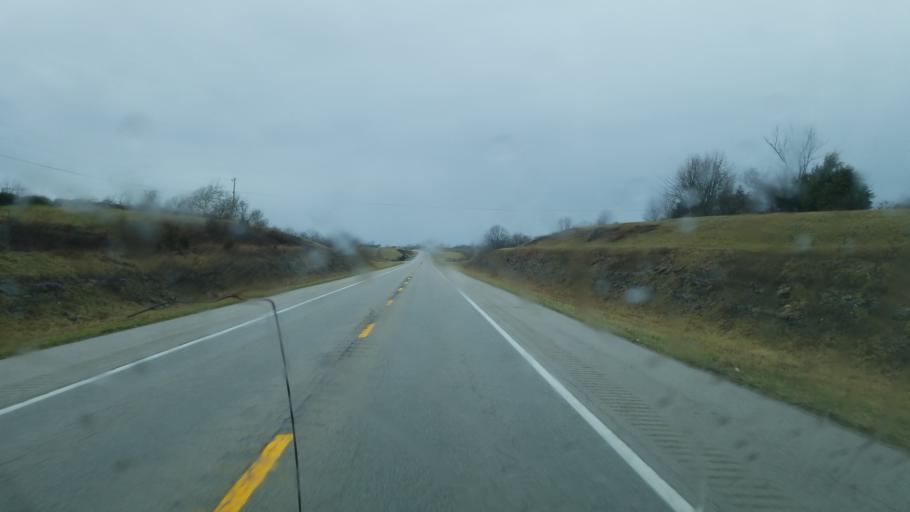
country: US
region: Ohio
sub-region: Adams County
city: Manchester
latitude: 38.5627
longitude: -83.6156
